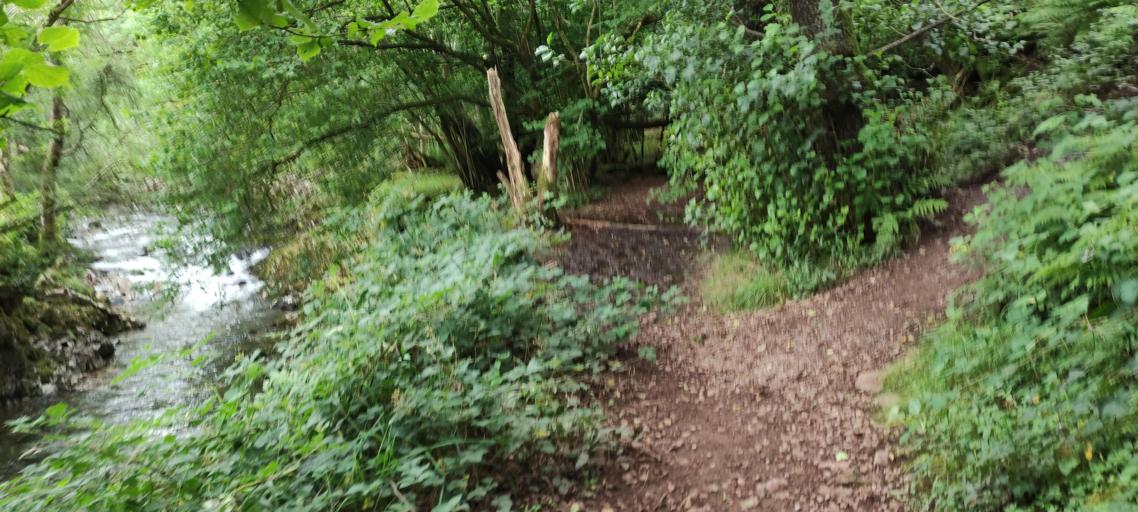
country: GB
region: England
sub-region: Cumbria
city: Millom
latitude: 54.3898
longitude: -3.2661
